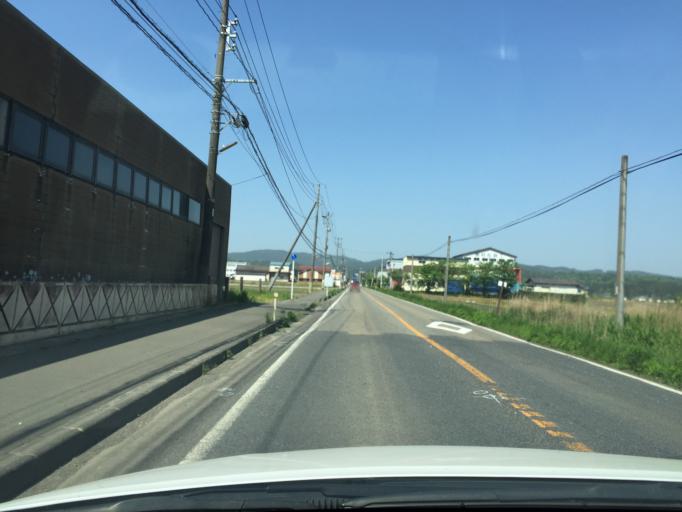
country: JP
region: Niigata
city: Muramatsu
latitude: 37.6876
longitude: 139.1569
